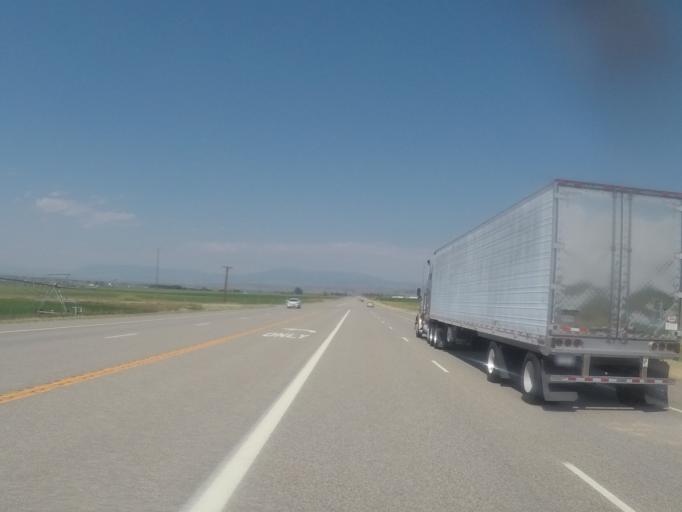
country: US
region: Montana
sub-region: Broadwater County
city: Townsend
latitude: 46.1208
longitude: -111.4974
